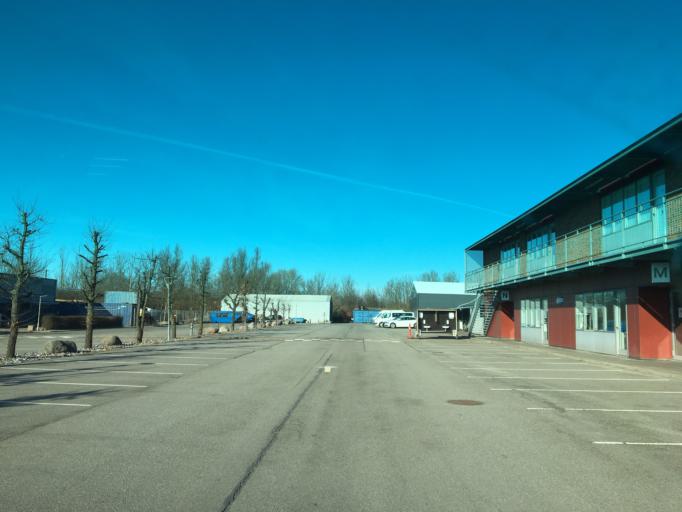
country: DK
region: Capital Region
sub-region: Hvidovre Kommune
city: Hvidovre
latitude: 55.6138
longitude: 12.4910
